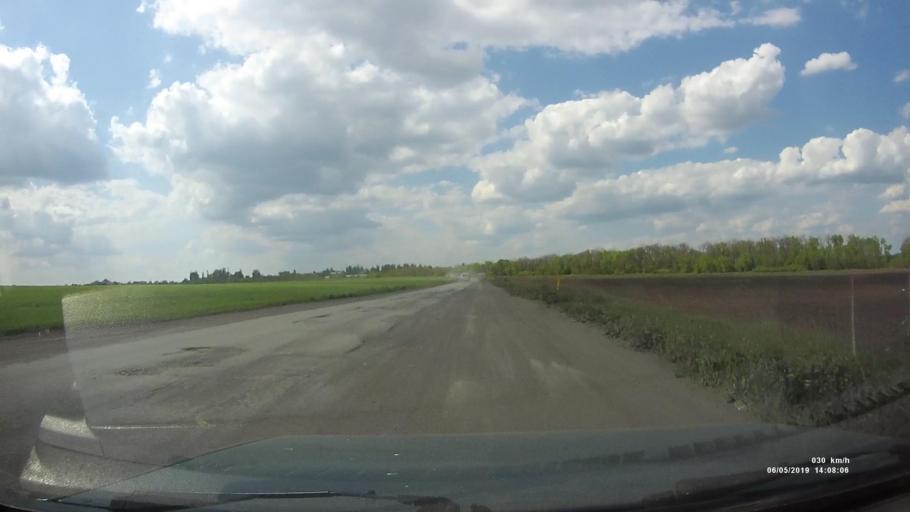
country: RU
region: Rostov
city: Shakhty
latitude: 47.6819
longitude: 40.3001
